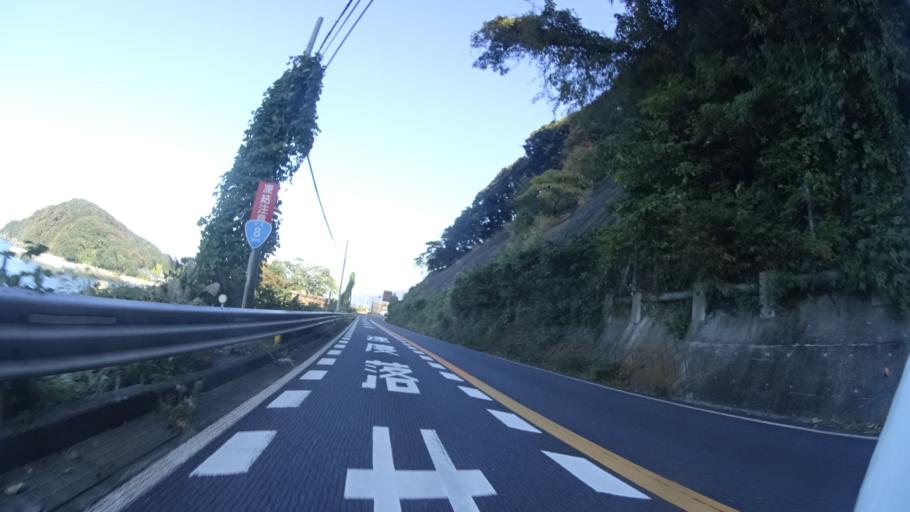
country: JP
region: Fukui
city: Tsuruga
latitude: 35.7337
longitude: 136.0979
